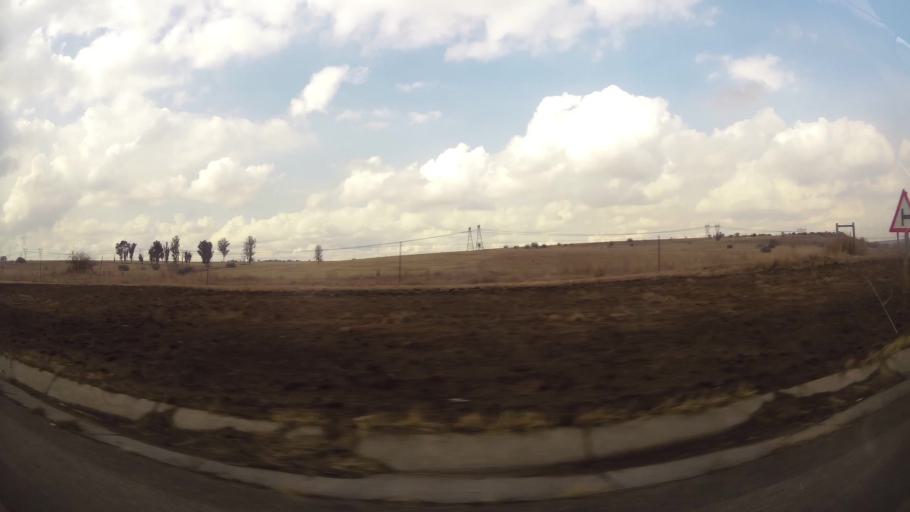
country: ZA
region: Orange Free State
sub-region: Fezile Dabi District Municipality
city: Sasolburg
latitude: -26.8013
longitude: 27.9135
